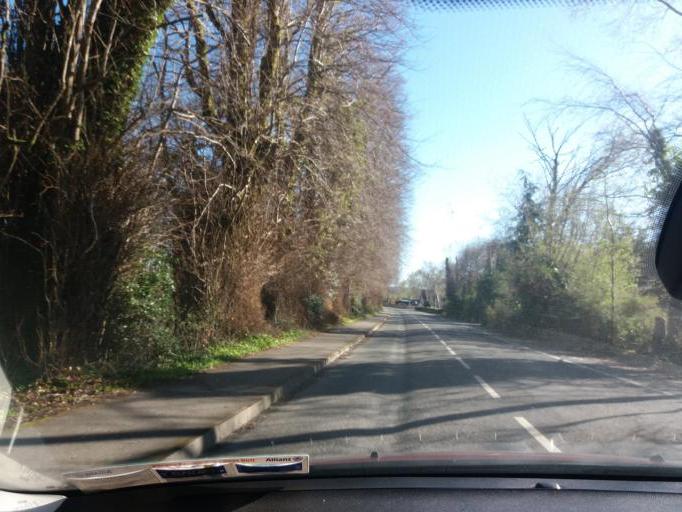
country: IE
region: Munster
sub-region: Ciarrai
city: Cill Airne
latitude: 52.0462
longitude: -9.5227
